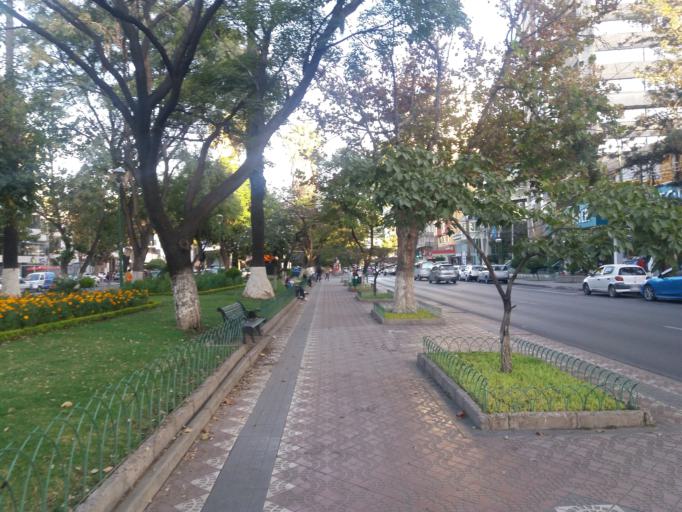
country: BO
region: Cochabamba
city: Cochabamba
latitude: -17.3859
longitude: -66.1572
